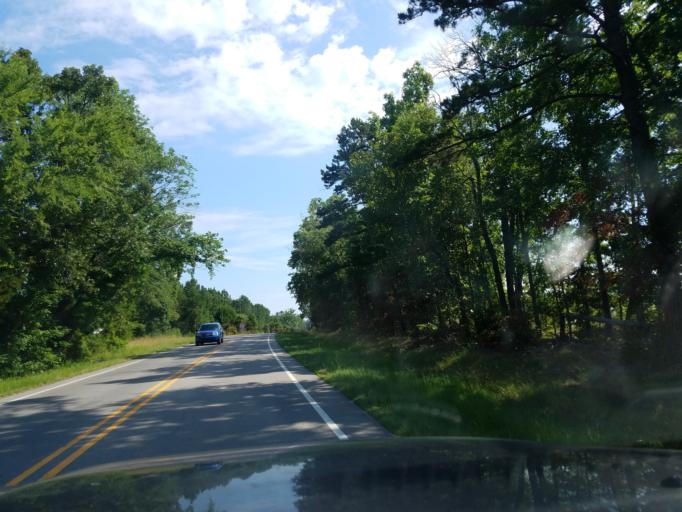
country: US
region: North Carolina
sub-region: Vance County
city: Henderson
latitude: 36.3702
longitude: -78.4190
